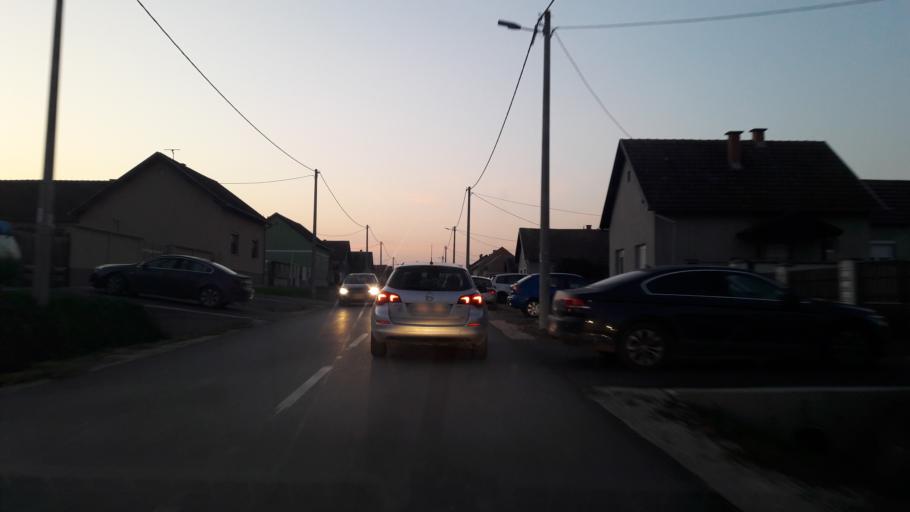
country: HR
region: Vukovarsko-Srijemska
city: Nijemci
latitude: 45.1412
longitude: 19.0357
